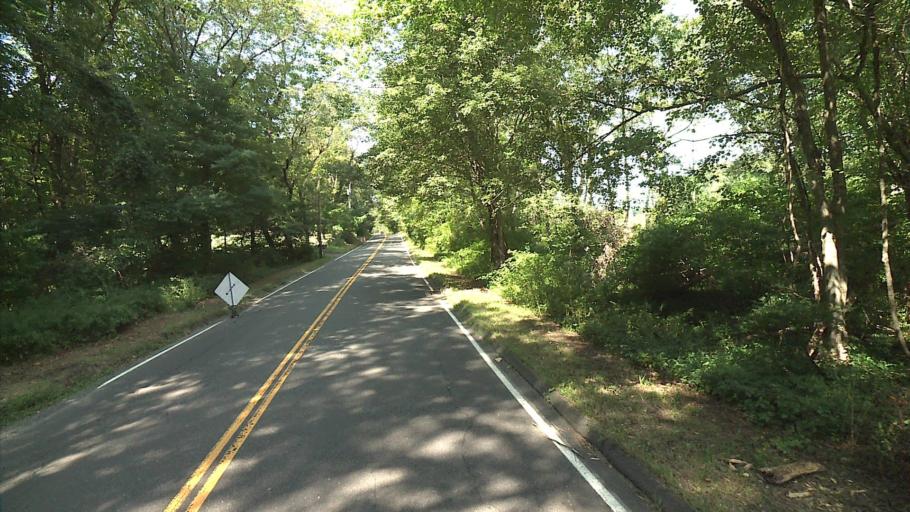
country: US
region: Connecticut
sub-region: Fairfield County
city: Westport
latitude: 41.2295
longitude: -73.3185
